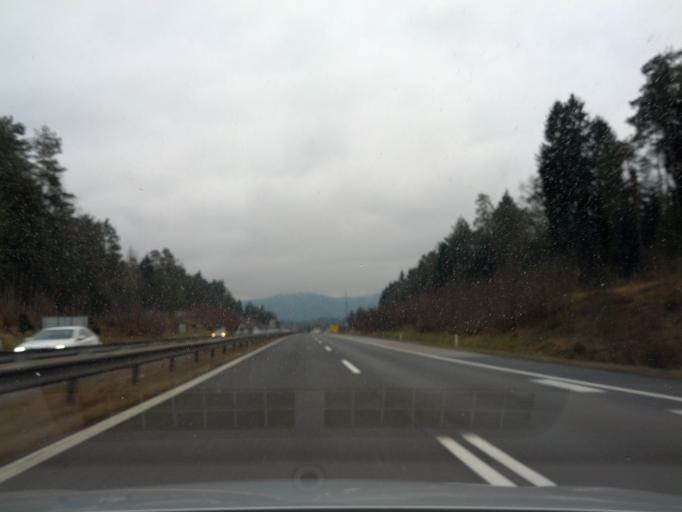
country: SI
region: Vodice
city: Vodice
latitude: 46.1925
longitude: 14.4754
